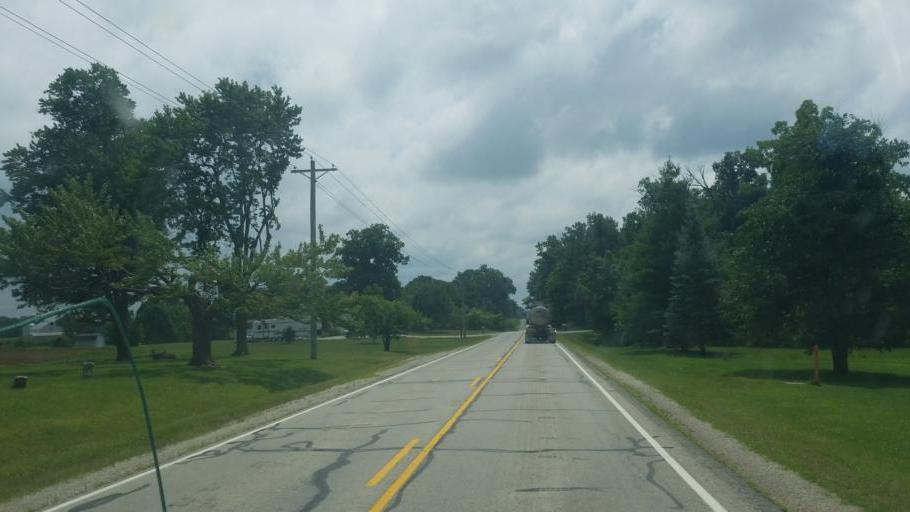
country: US
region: Indiana
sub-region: Huntington County
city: Warren
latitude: 40.6702
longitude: -85.4133
